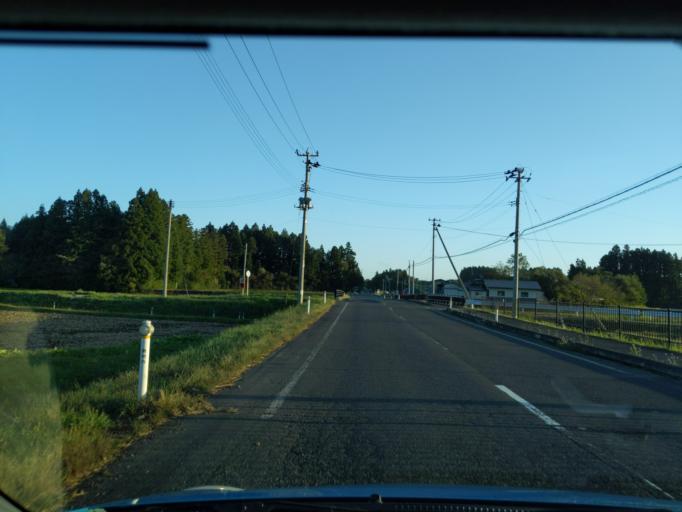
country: JP
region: Iwate
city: Mizusawa
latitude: 39.0780
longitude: 141.0931
